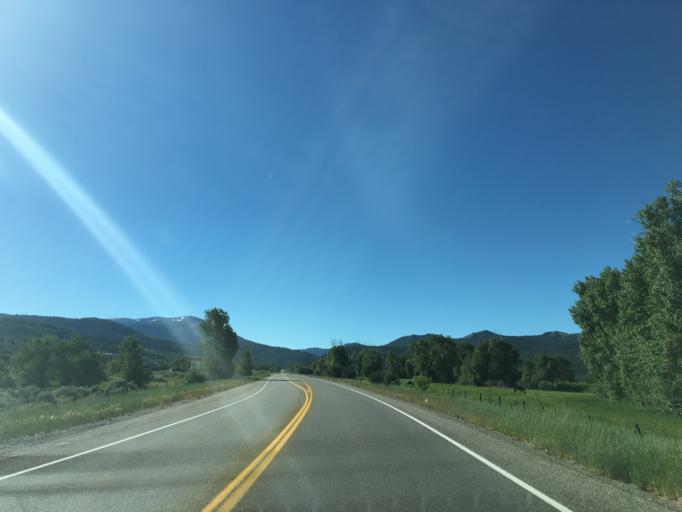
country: US
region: Idaho
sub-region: Teton County
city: Victor
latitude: 43.5961
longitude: -111.1101
